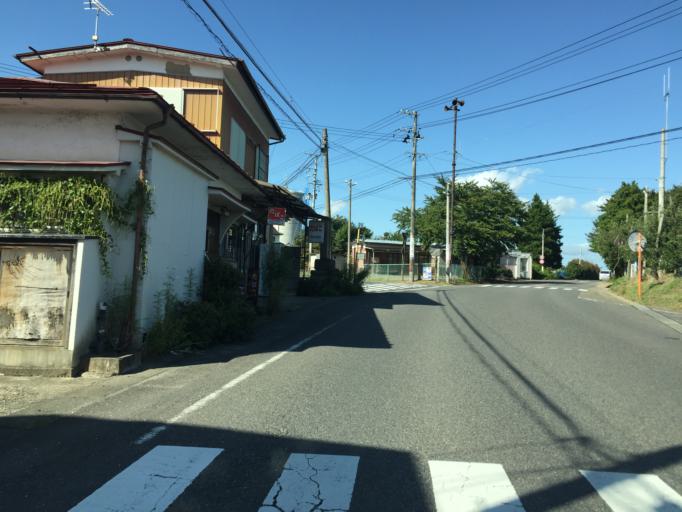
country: JP
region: Fukushima
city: Sukagawa
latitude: 37.2694
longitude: 140.3813
